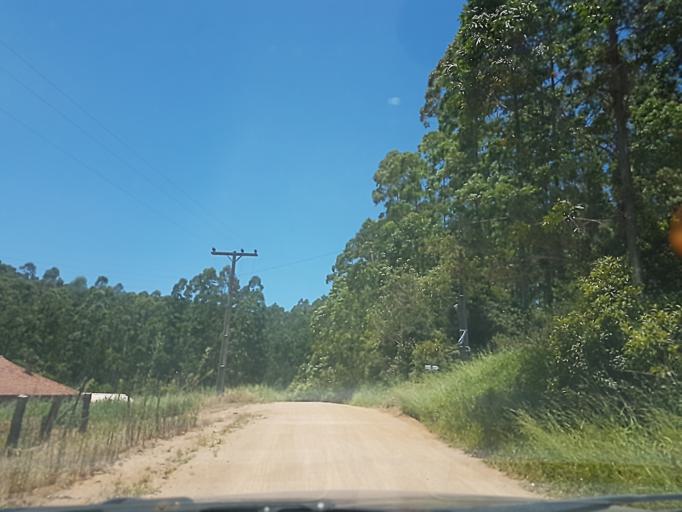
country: BR
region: Santa Catarina
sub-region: Braco Do Norte
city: Braco do Norte
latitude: -28.3909
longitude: -49.1276
